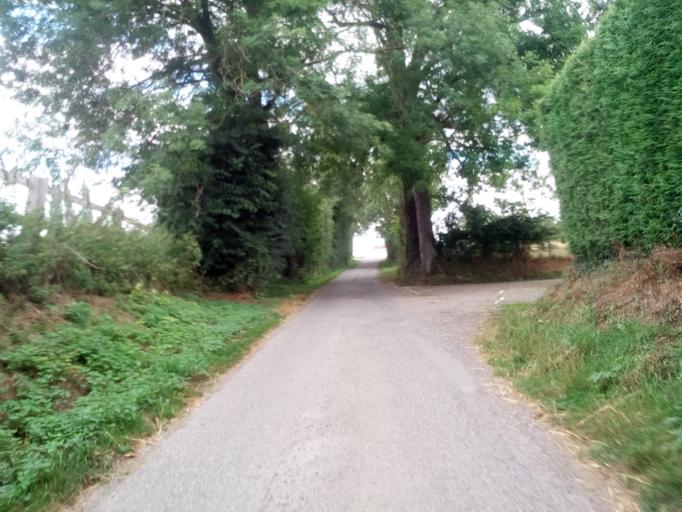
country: FR
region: Lower Normandy
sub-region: Departement du Calvados
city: Troarn
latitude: 49.1689
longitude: -0.1418
